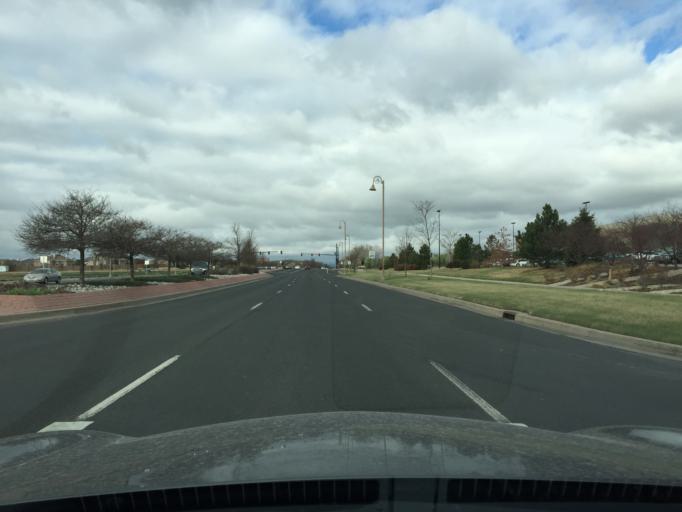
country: US
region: Colorado
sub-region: Adams County
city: Northglenn
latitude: 39.9577
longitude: -104.9939
